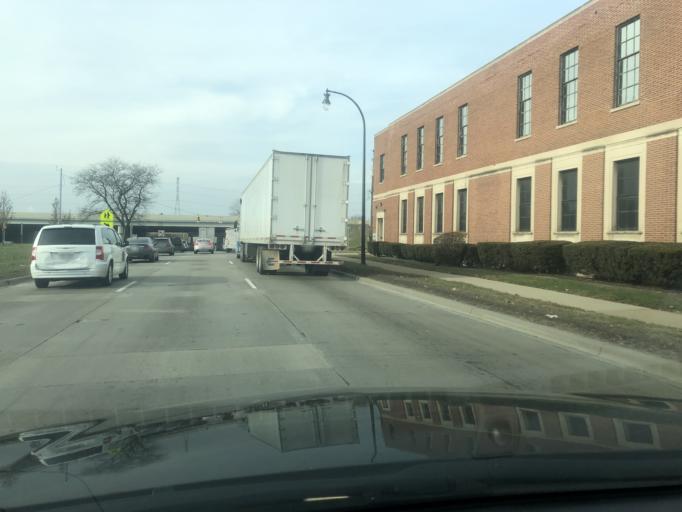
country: US
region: Michigan
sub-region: Wayne County
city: Lincoln Park
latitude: 42.2523
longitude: -83.1836
